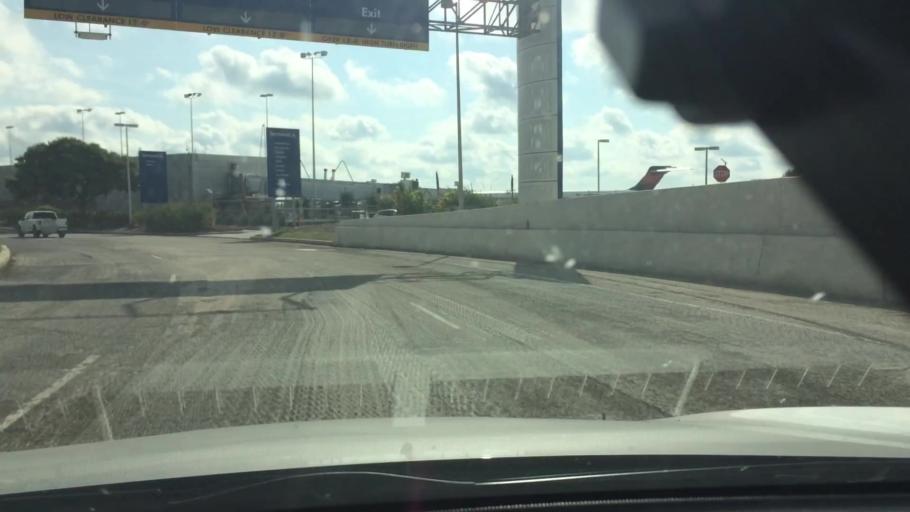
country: US
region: Texas
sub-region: Bexar County
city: Alamo Heights
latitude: 29.5247
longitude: -98.4747
